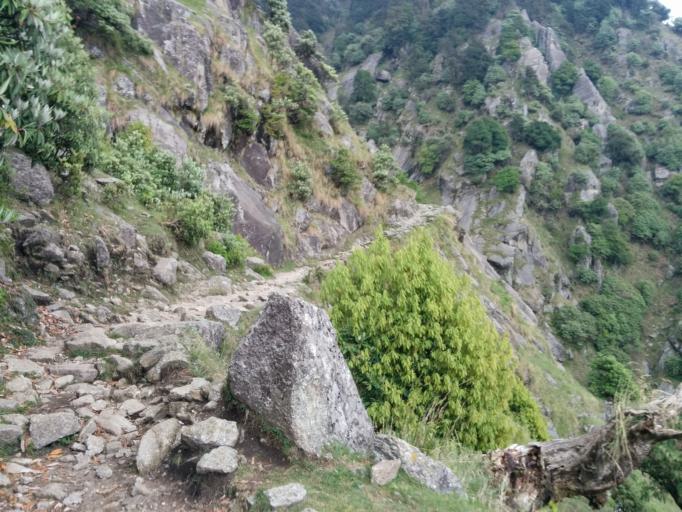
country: IN
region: Himachal Pradesh
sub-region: Kangra
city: Dharmsala
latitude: 32.2579
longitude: 76.3438
